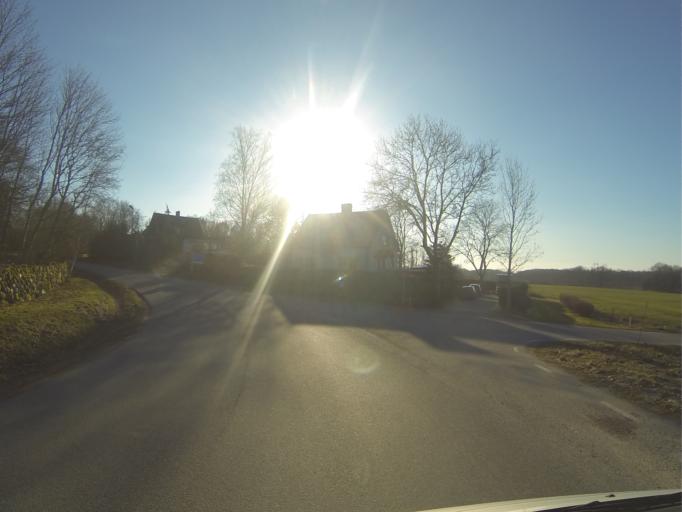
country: SE
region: Skane
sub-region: Horby Kommun
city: Hoerby
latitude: 55.8391
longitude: 13.6249
